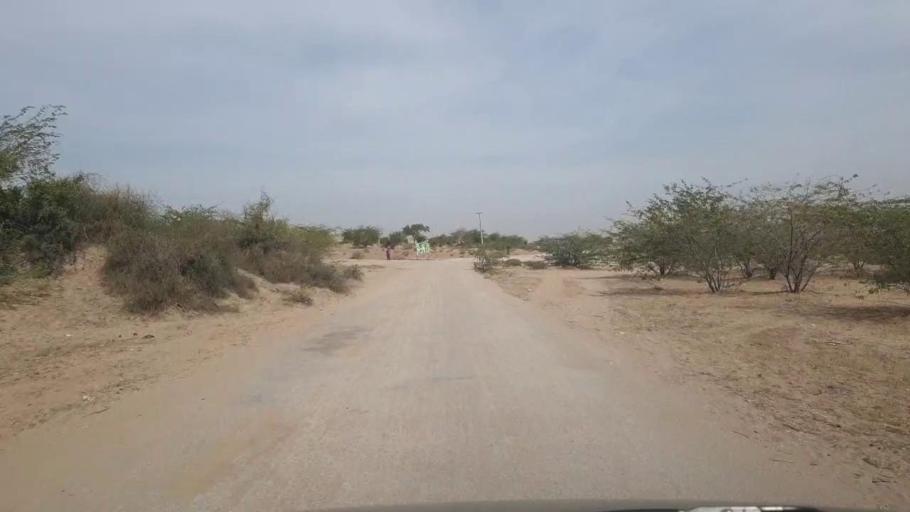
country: PK
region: Sindh
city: Umarkot
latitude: 25.2959
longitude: 69.7277
